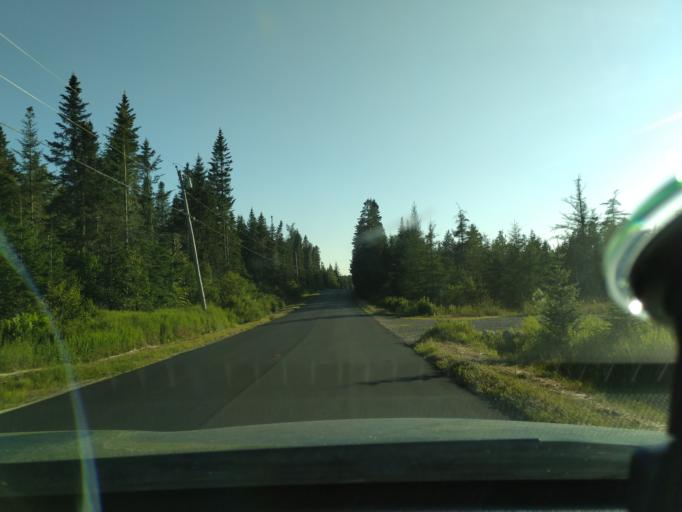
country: US
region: Maine
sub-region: Washington County
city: Machiasport
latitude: 44.6695
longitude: -67.1970
